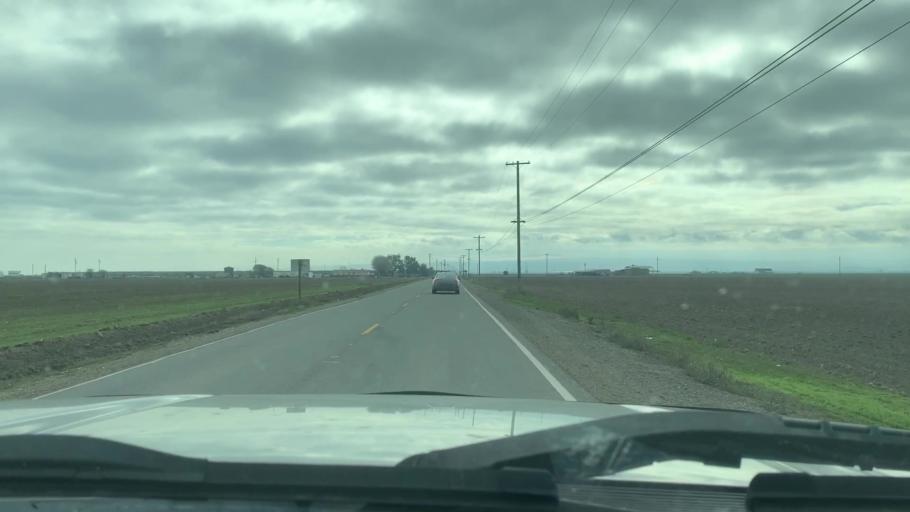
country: US
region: California
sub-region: Merced County
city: Los Banos
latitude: 37.0316
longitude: -120.8360
